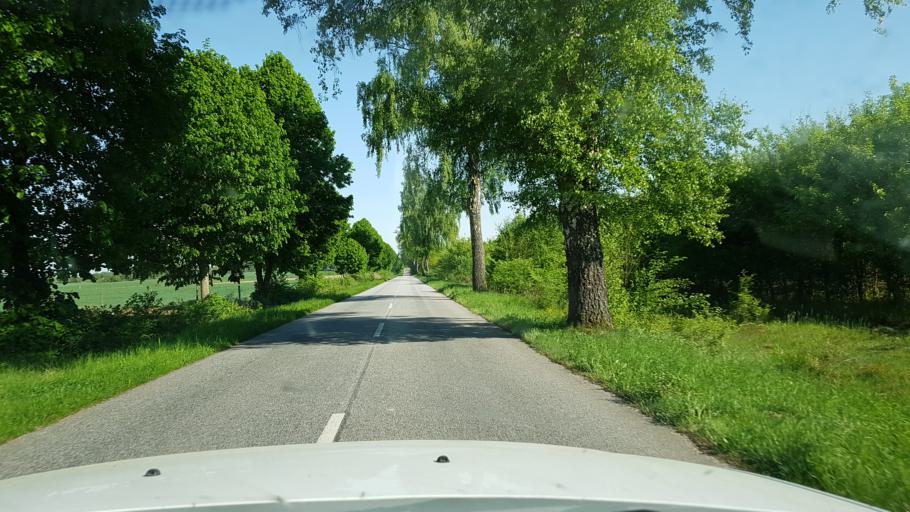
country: PL
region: West Pomeranian Voivodeship
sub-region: Powiat lobeski
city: Resko
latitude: 53.8156
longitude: 15.3995
